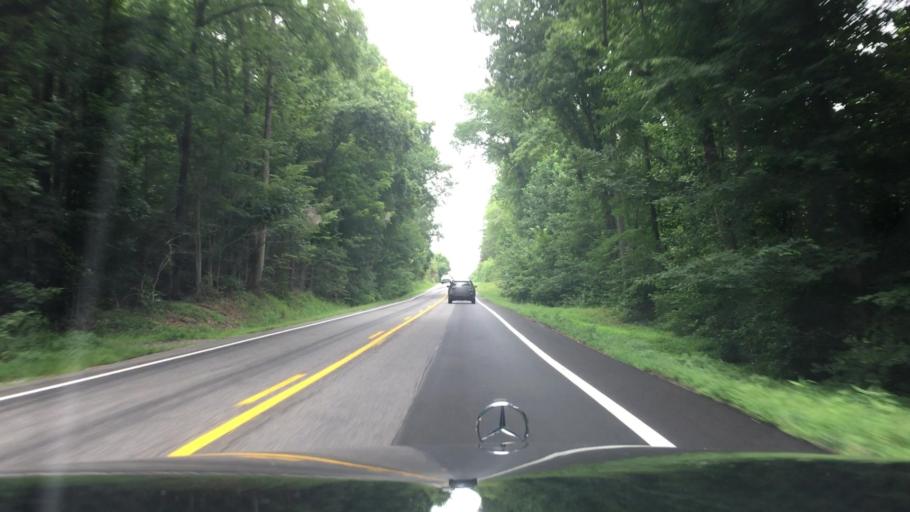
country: US
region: Virginia
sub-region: Prince Edward County
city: Farmville
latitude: 37.2737
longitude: -78.2628
